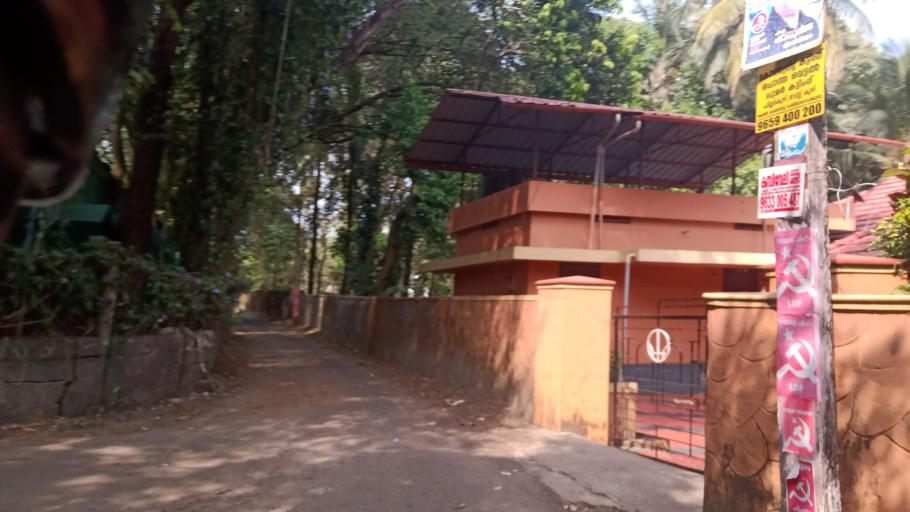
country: IN
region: Kerala
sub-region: Palakkad district
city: Cherpulassery
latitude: 10.8816
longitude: 76.3135
